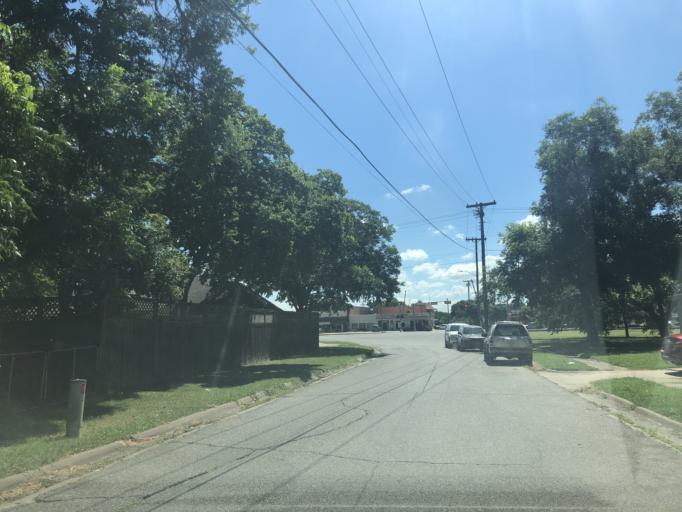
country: US
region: Texas
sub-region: Dallas County
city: Duncanville
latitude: 32.6547
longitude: -96.9094
